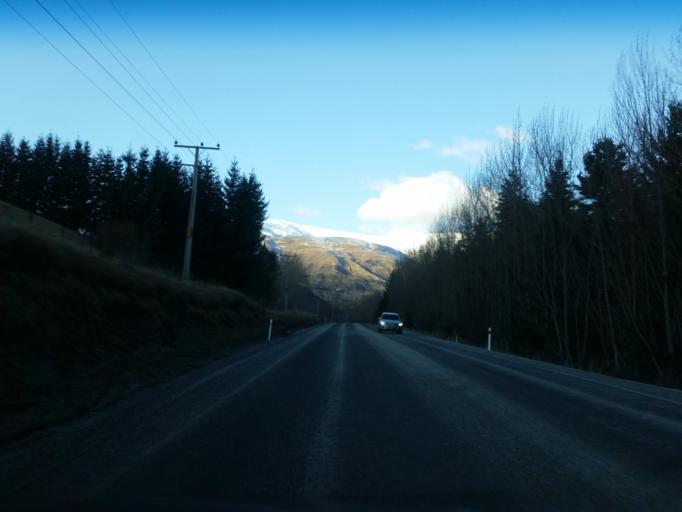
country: NZ
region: Otago
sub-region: Queenstown-Lakes District
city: Arrowtown
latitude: -44.9457
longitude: 168.7974
